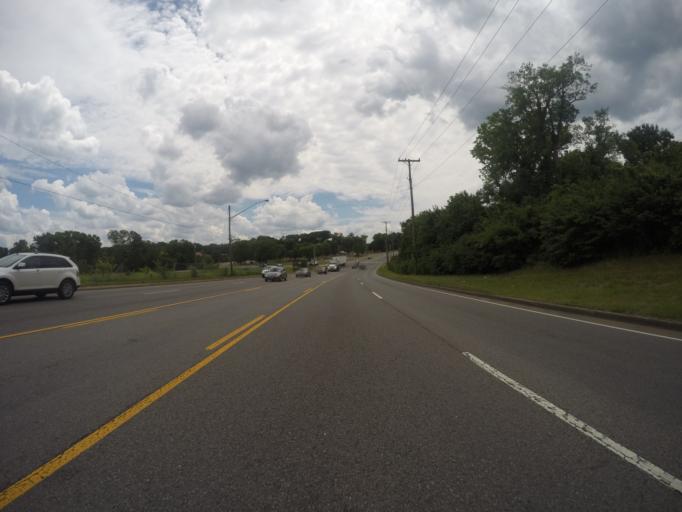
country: US
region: Tennessee
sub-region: Davidson County
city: Lakewood
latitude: 36.2333
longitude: -86.6252
